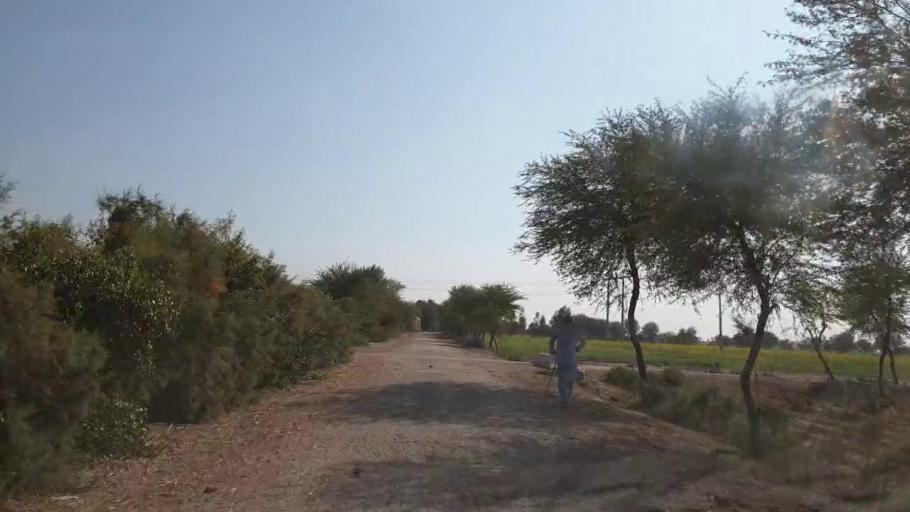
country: PK
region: Sindh
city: Mirpur Khas
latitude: 25.7204
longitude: 69.1553
